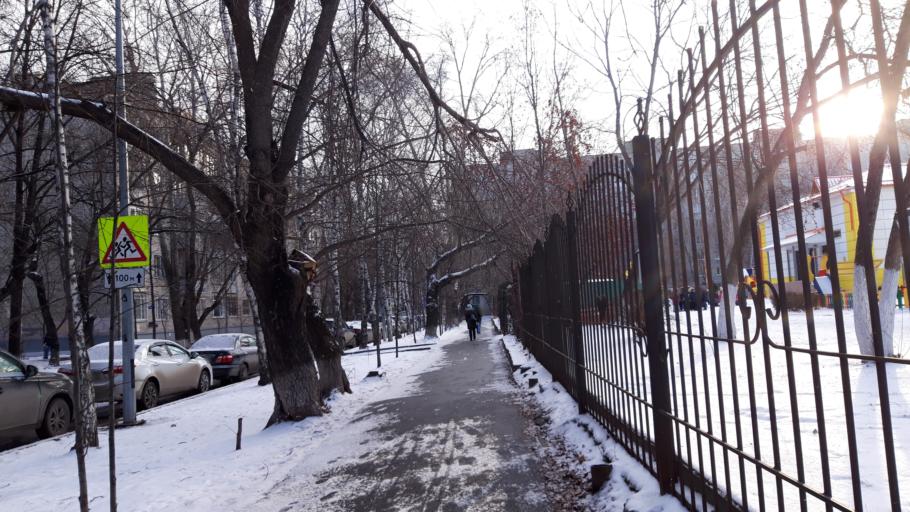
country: RU
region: Tjumen
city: Tyumen
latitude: 57.1513
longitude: 65.5502
